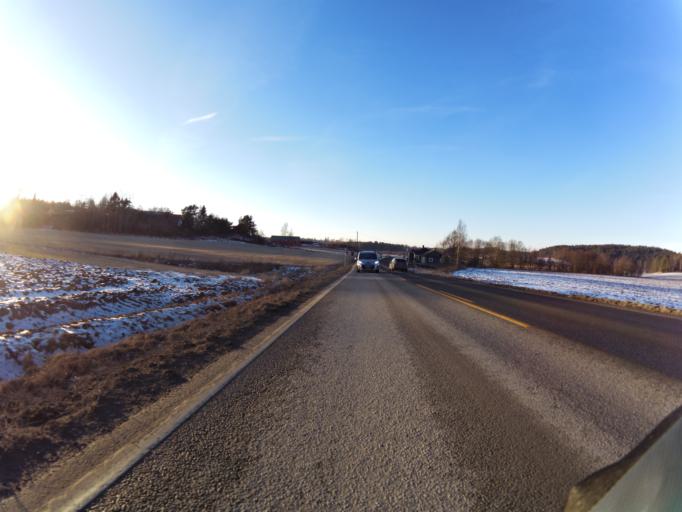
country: NO
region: Ostfold
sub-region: Fredrikstad
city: Fredrikstad
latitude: 59.2503
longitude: 10.8789
